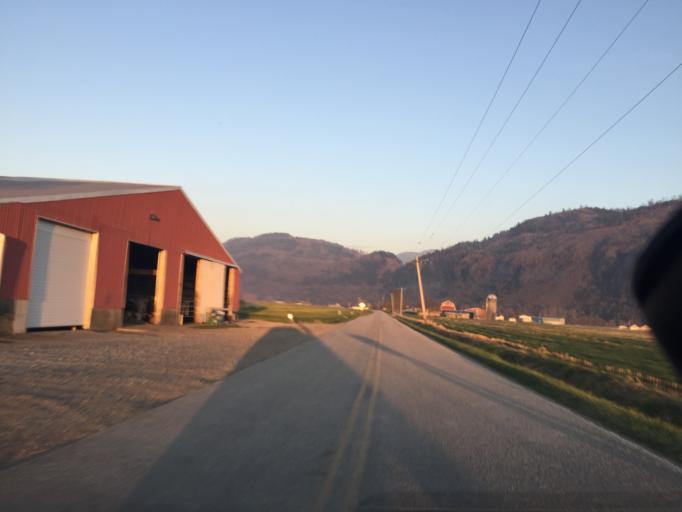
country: US
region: Washington
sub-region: Whatcom County
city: Sumas
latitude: 48.9998
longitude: -122.1943
